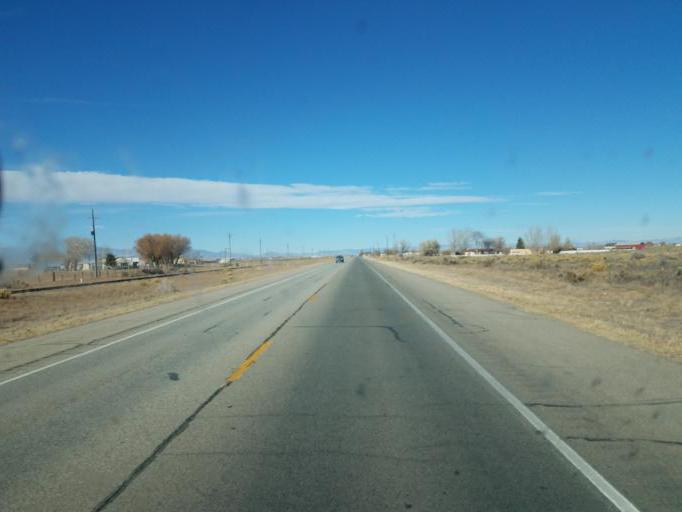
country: US
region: Colorado
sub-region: Alamosa County
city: Alamosa
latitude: 37.5008
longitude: -105.9550
